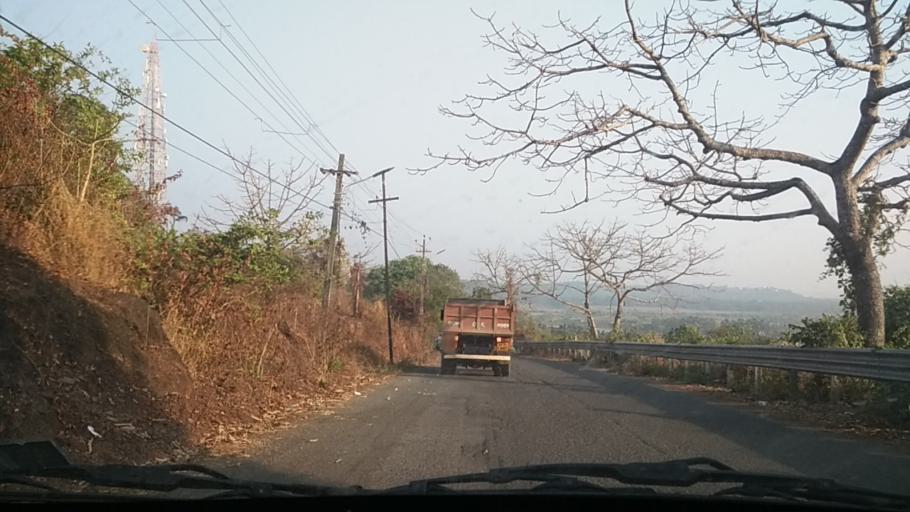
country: IN
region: Goa
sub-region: North Goa
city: Goa Velha
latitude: 15.4628
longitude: 73.8771
